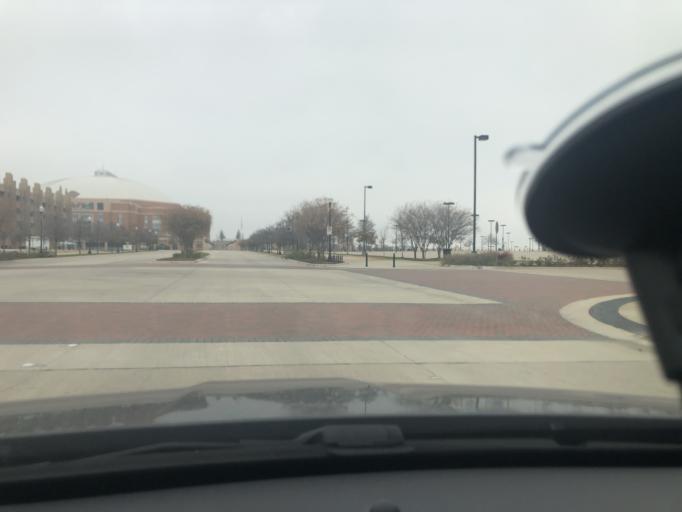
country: US
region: Texas
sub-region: Tarrant County
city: Westworth
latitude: 32.7375
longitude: -97.3677
